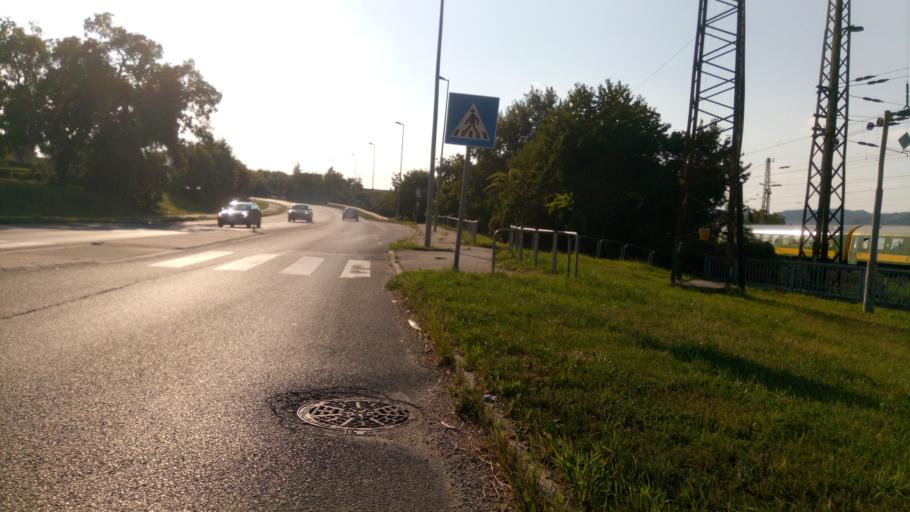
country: HU
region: Pest
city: Budaors
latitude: 47.4475
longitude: 18.9619
